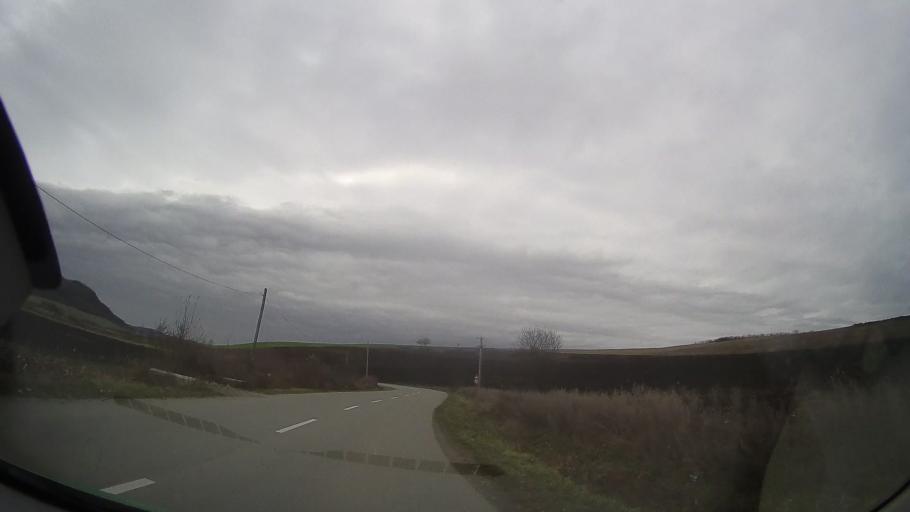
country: RO
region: Bistrita-Nasaud
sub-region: Comuna Milas
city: Milas
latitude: 46.8041
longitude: 24.4278
